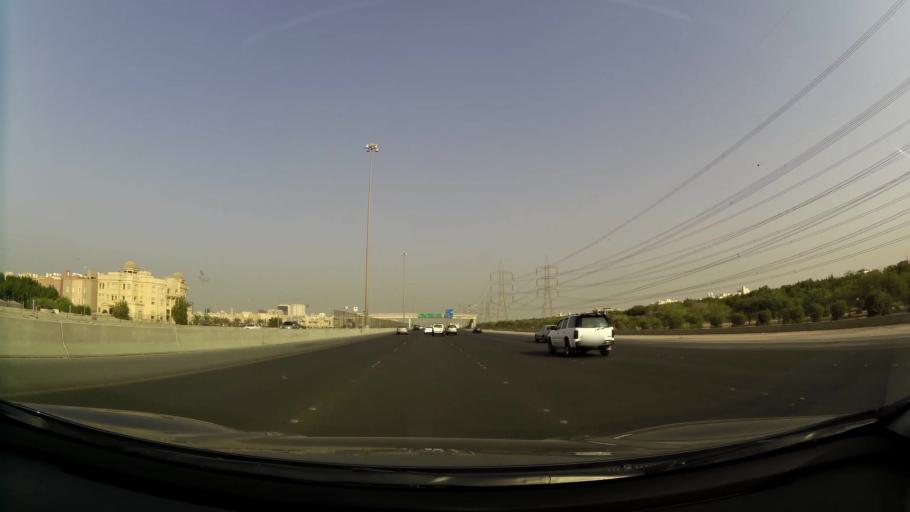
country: KW
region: Al Asimah
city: Ar Rabiyah
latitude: 29.2979
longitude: 47.8972
